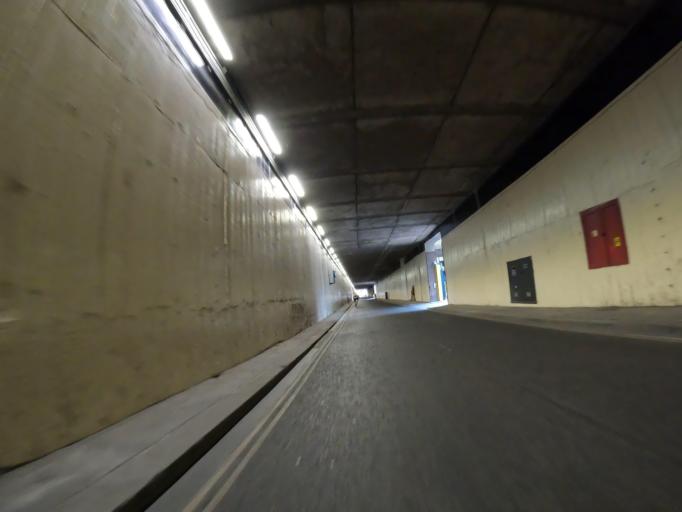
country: GB
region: England
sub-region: Greater London
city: Bethnal Green
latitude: 51.5457
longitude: -0.0778
